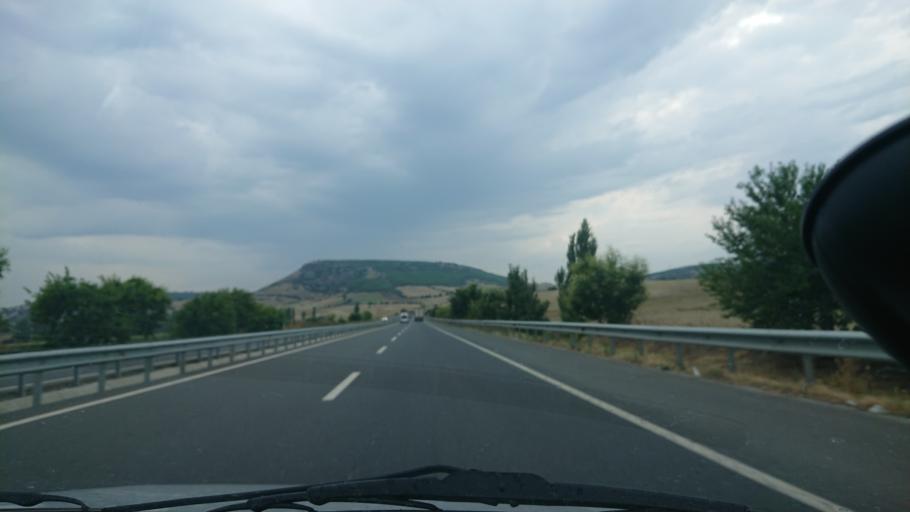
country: TR
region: Manisa
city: Selendi
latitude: 38.6186
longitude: 28.8811
